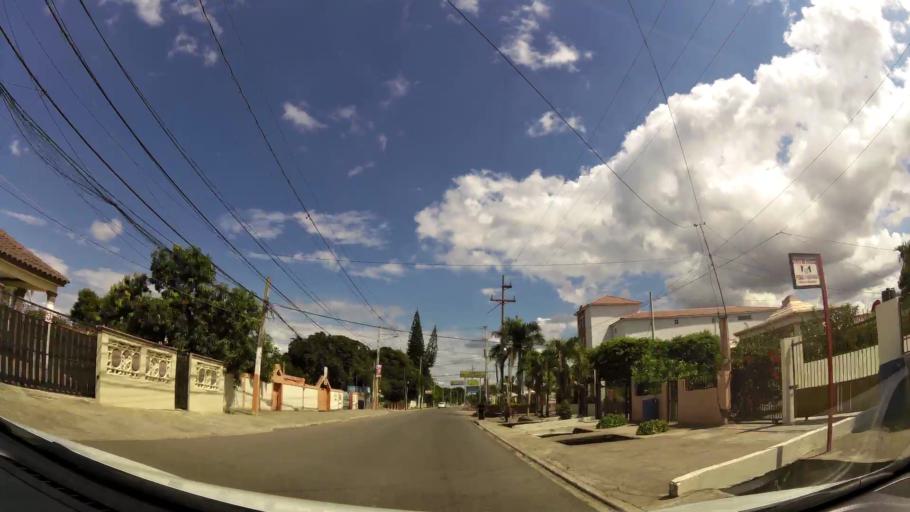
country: DO
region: Santiago
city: Licey al Medio
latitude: 19.3829
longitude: -70.6212
